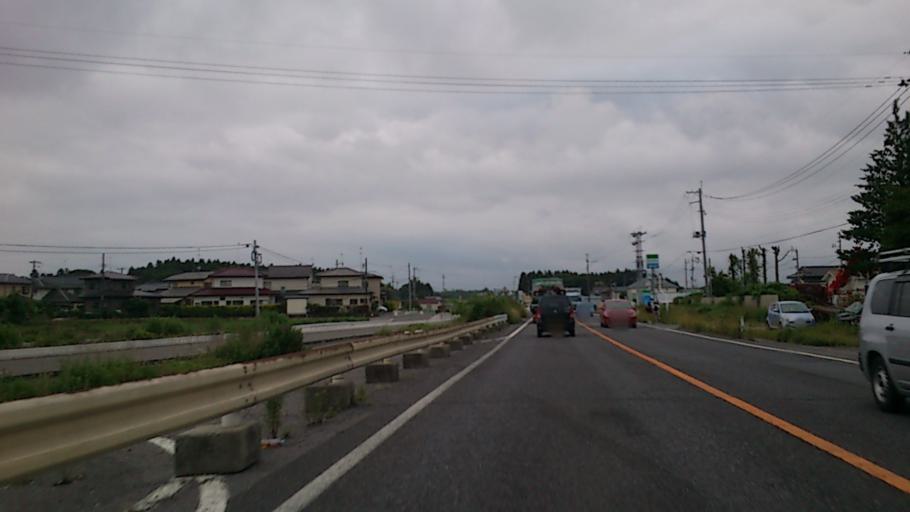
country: JP
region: Fukushima
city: Sukagawa
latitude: 37.2508
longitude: 140.3398
